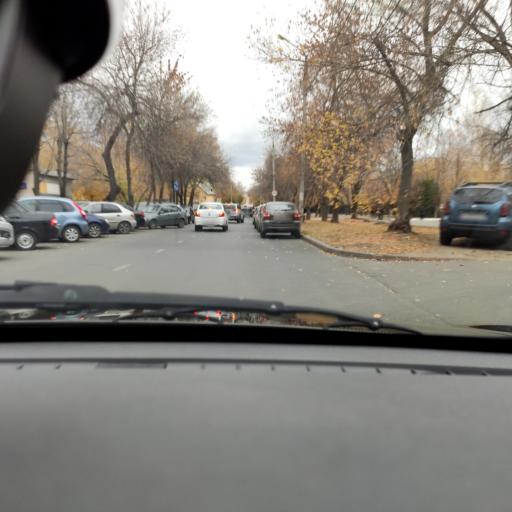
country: RU
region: Samara
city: Tol'yatti
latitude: 53.4995
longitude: 49.3962
